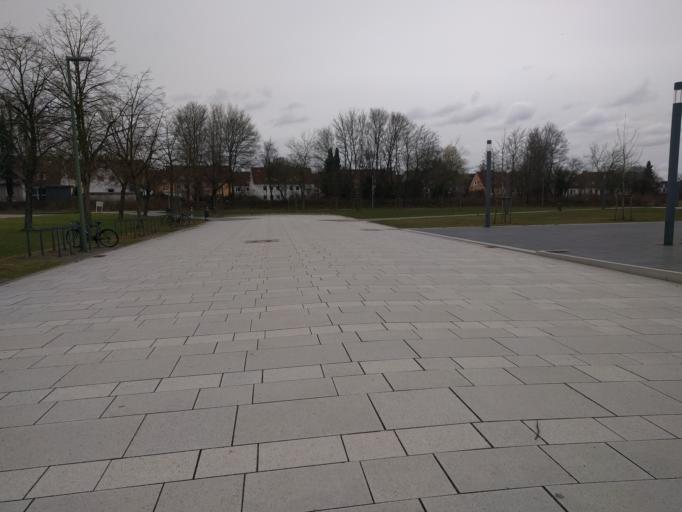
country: DE
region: North Rhine-Westphalia
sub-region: Regierungsbezirk Detmold
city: Bielefeld
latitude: 52.0404
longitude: 8.4913
